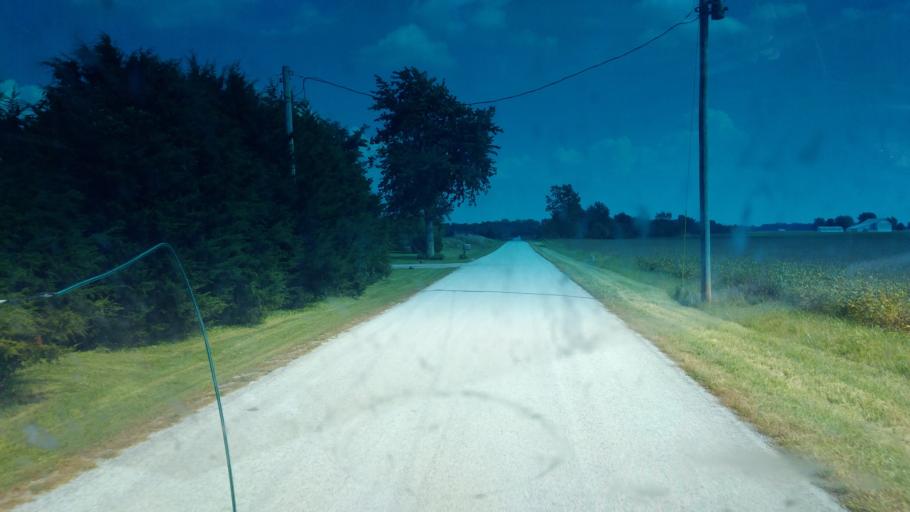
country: US
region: Ohio
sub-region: Hardin County
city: Kenton
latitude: 40.6606
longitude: -83.6831
